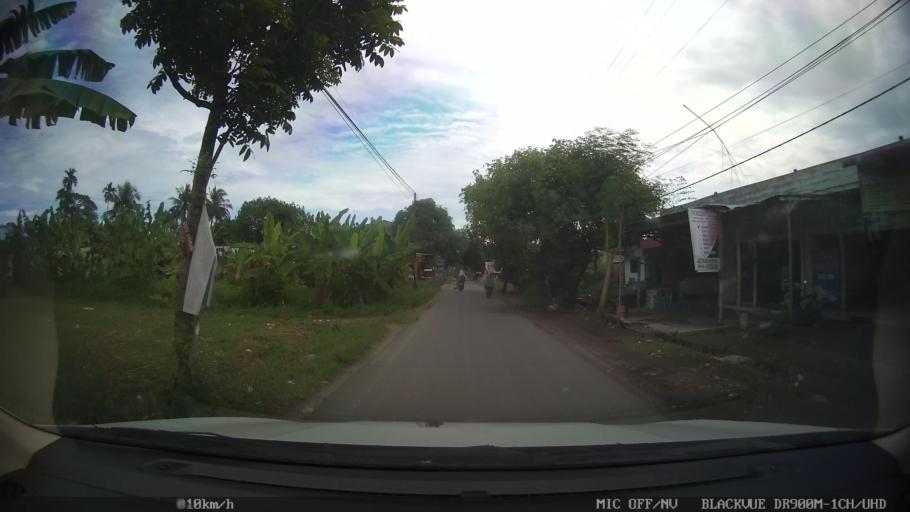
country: ID
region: North Sumatra
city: Sunggal
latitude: 3.5791
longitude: 98.5649
